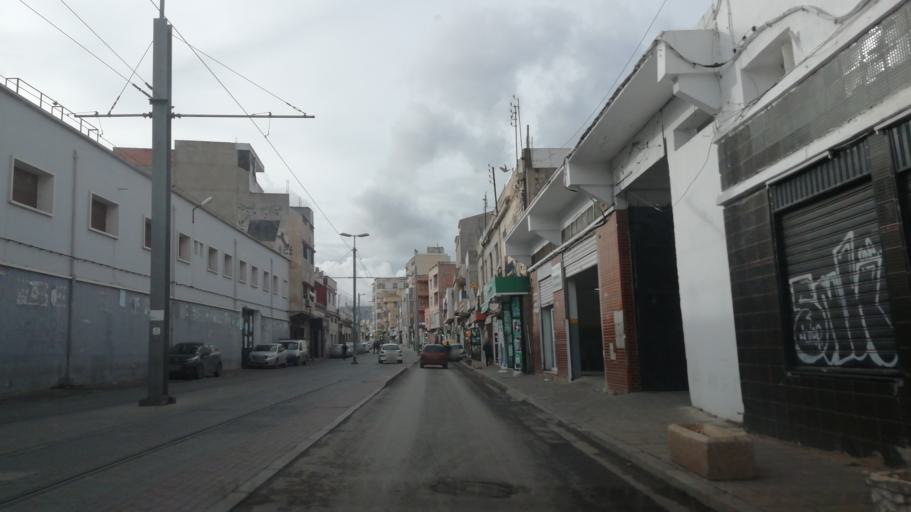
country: DZ
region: Oran
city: Oran
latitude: 35.6984
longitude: -0.6196
